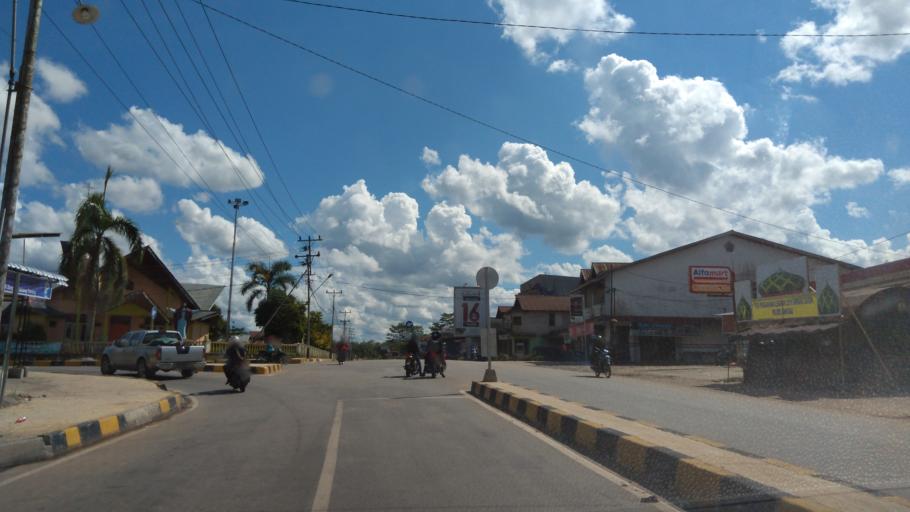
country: ID
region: West Kalimantan
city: Tayan
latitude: 0.2931
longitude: 110.2355
